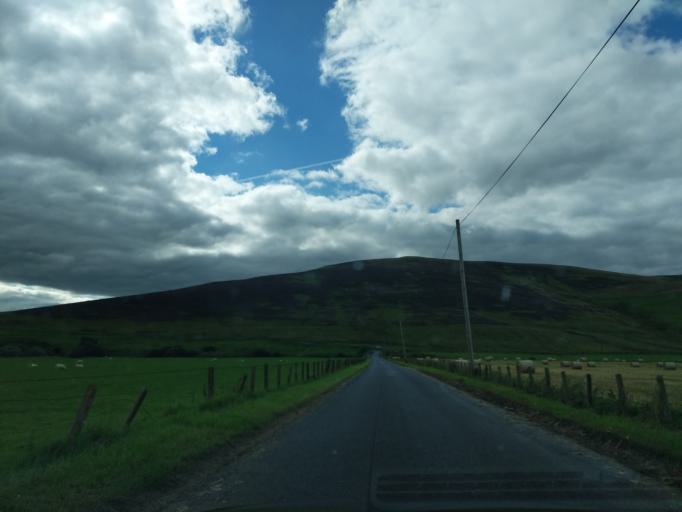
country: GB
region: Scotland
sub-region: The Scottish Borders
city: West Linton
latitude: 55.6753
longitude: -3.3308
